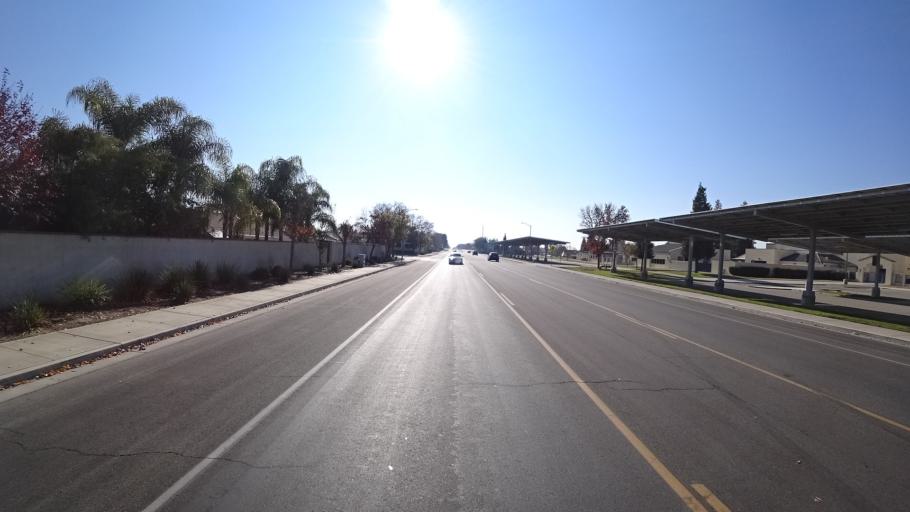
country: US
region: California
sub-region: Kern County
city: Greenacres
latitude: 35.3139
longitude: -119.1188
